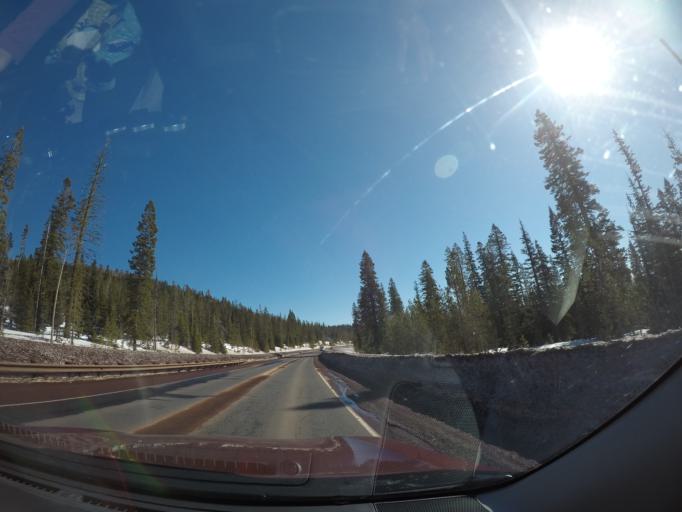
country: US
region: Oregon
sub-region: Deschutes County
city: Sunriver
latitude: 43.9839
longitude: -121.6032
